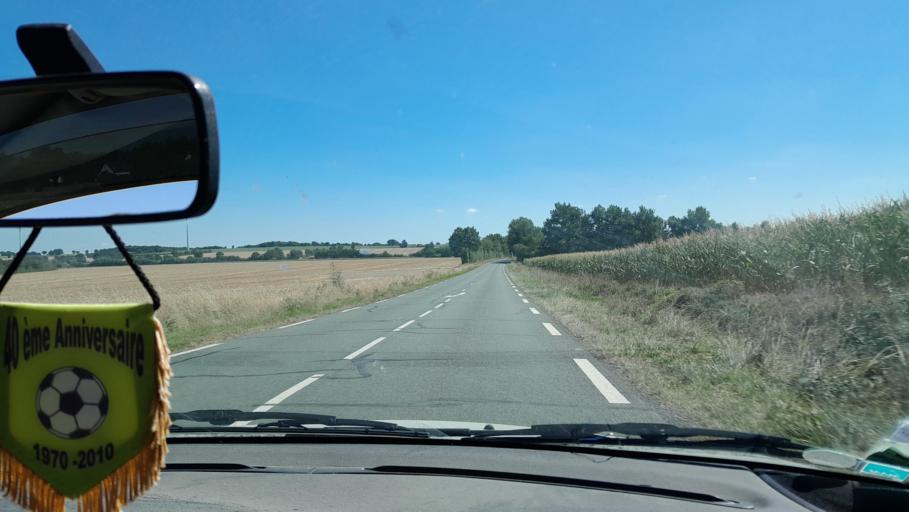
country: FR
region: Pays de la Loire
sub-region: Departement de la Loire-Atlantique
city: Saint-Mars-la-Jaille
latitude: 47.5675
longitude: -1.1883
